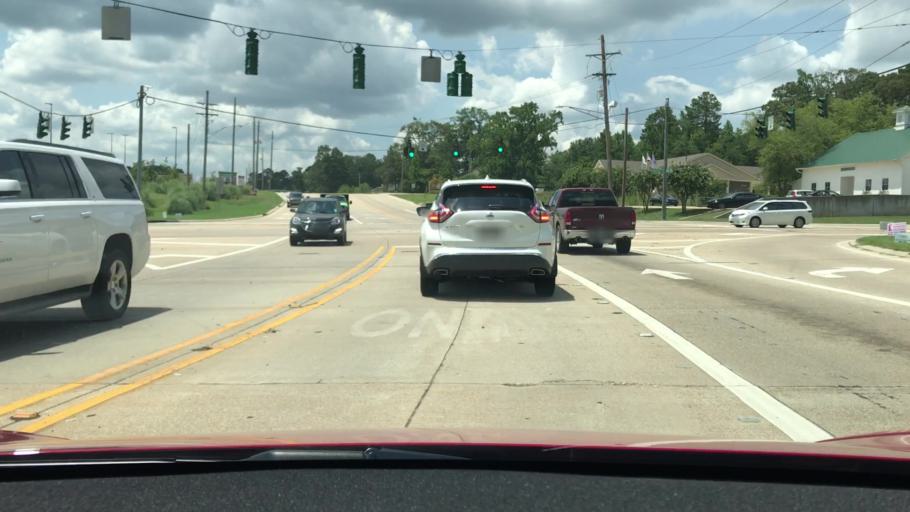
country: US
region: Louisiana
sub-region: Bossier Parish
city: Bossier City
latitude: 32.3943
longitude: -93.7251
